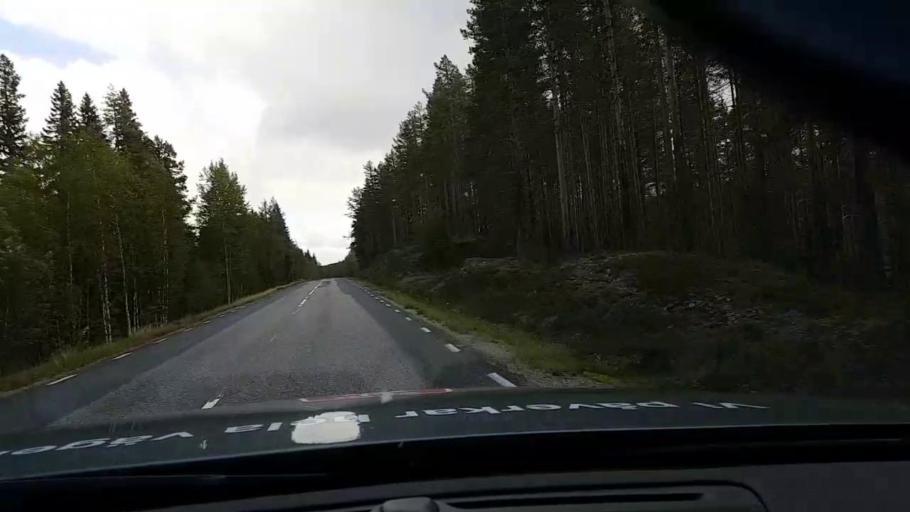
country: SE
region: Vaesterbotten
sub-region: Asele Kommun
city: Asele
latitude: 63.8424
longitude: 17.4250
